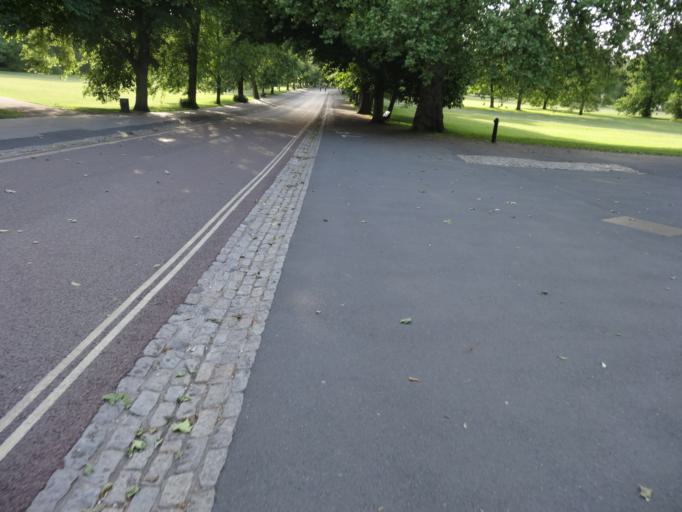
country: GB
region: England
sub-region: Greater London
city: Blackheath
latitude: 51.4779
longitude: -0.0035
